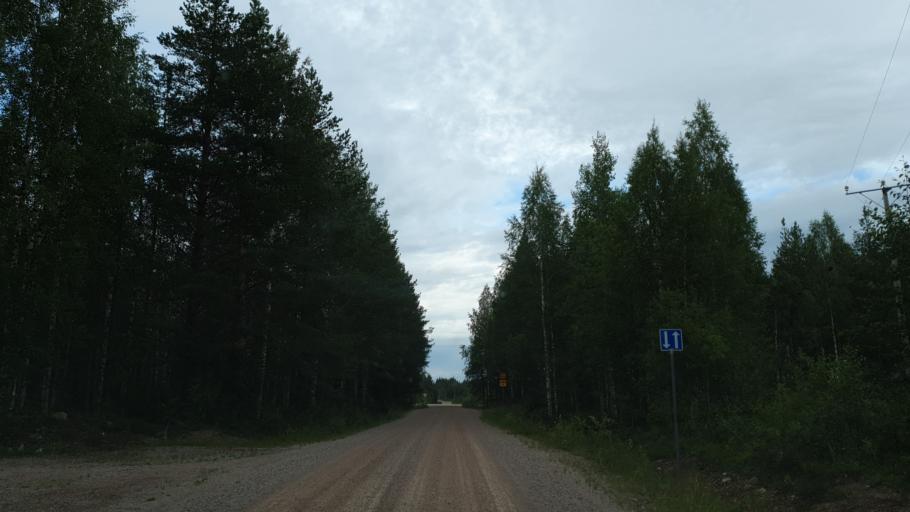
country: FI
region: Kainuu
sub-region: Kehys-Kainuu
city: Suomussalmi
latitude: 64.4534
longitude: 28.9762
